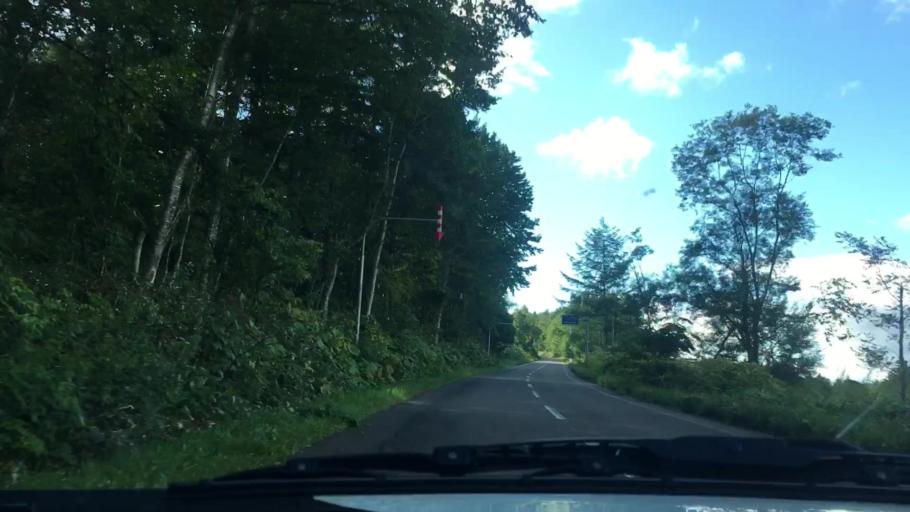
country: JP
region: Hokkaido
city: Otofuke
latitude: 43.1710
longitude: 142.9765
